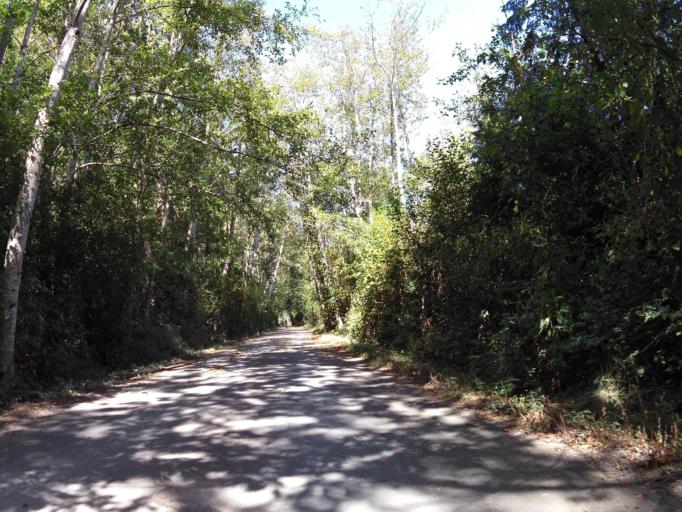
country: CA
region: British Columbia
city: Victoria
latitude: 48.5483
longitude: -123.3853
